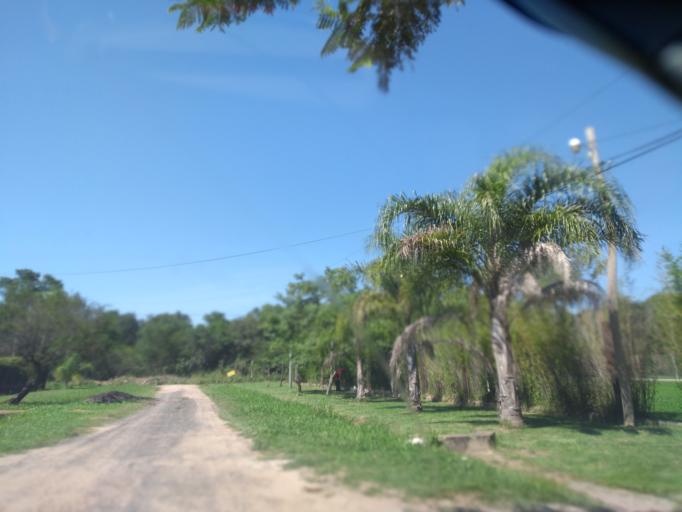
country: AR
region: Chaco
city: Resistencia
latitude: -27.4320
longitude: -58.9422
